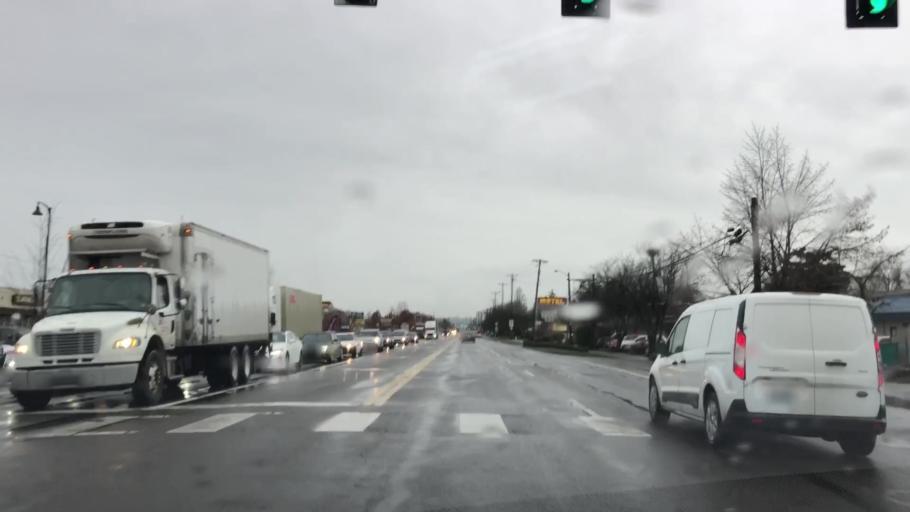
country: US
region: Washington
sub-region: Pierce County
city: Fife
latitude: 47.2431
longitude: -122.3649
